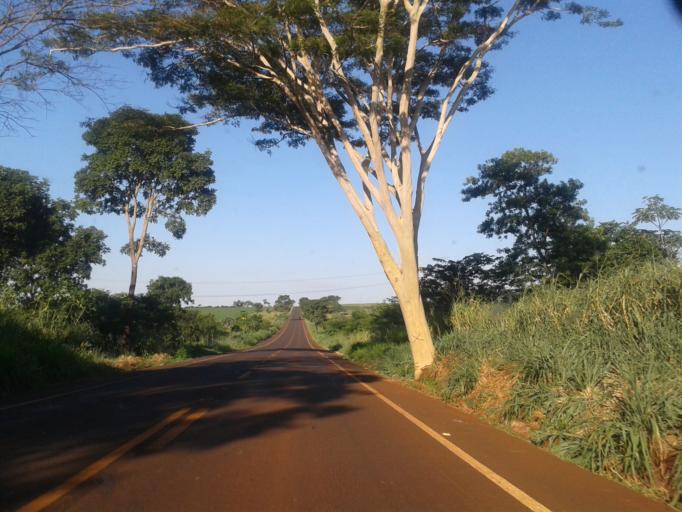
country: BR
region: Minas Gerais
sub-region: Capinopolis
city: Capinopolis
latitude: -18.7120
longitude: -49.7884
